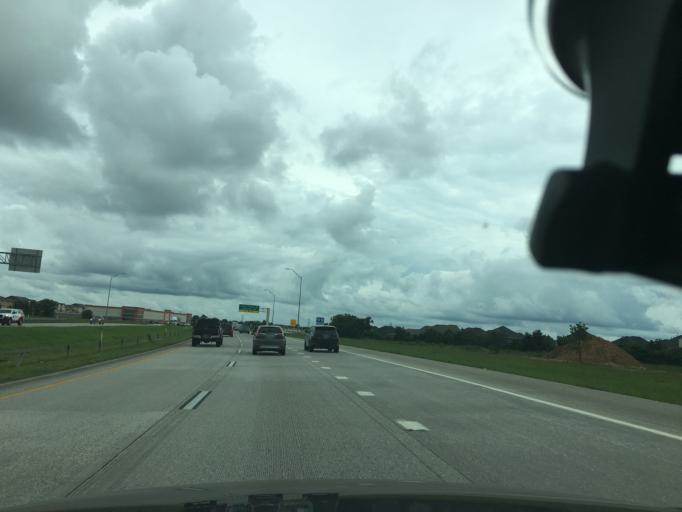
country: US
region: Texas
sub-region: Harris County
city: Tomball
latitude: 30.0801
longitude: -95.5391
